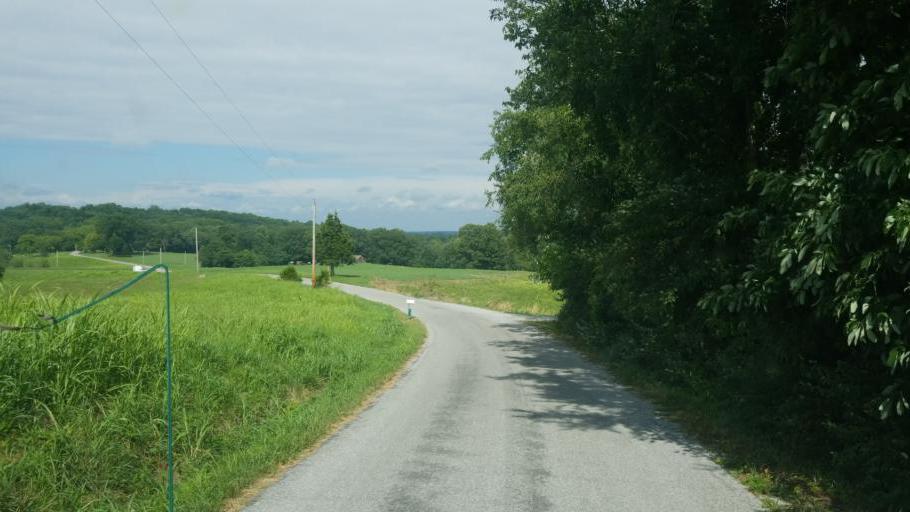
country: US
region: Illinois
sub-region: Union County
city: Cobden
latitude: 37.6035
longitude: -89.3664
